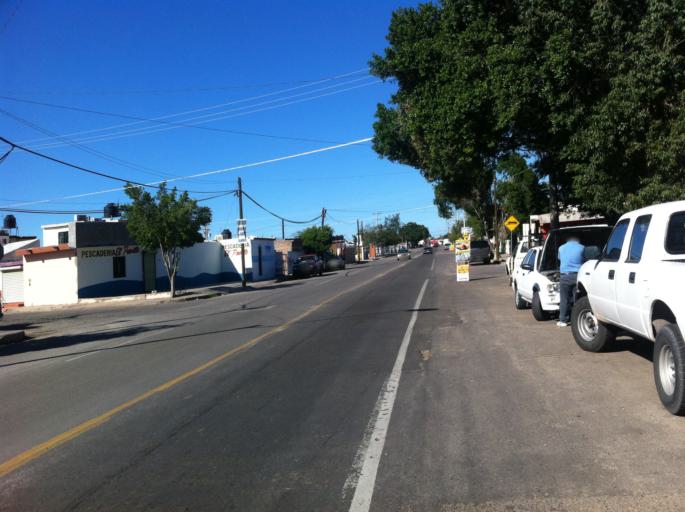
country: MX
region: Sonora
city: Hermosillo
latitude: 29.0996
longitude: -111.0049
